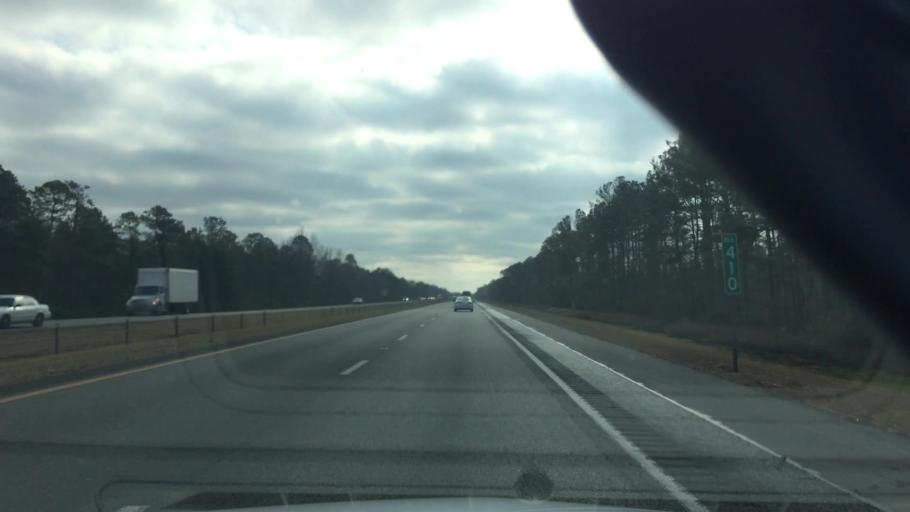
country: US
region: North Carolina
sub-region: Pender County
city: Rocky Point
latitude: 34.4134
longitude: -77.8700
